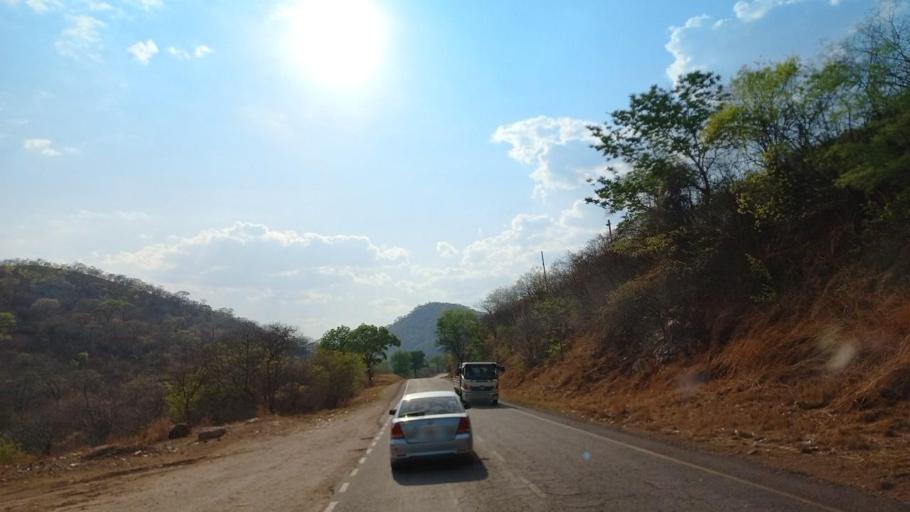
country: ZM
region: Lusaka
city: Luangwa
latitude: -14.9855
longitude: 30.1959
